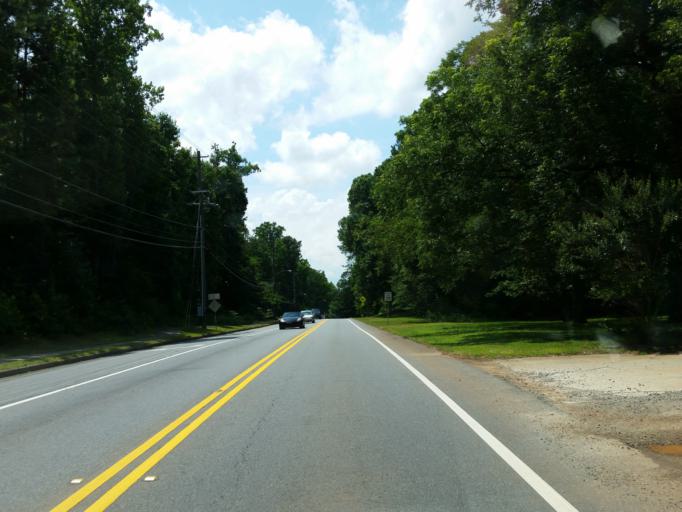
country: US
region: Georgia
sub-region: Fulton County
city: Roswell
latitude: 34.0261
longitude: -84.3856
